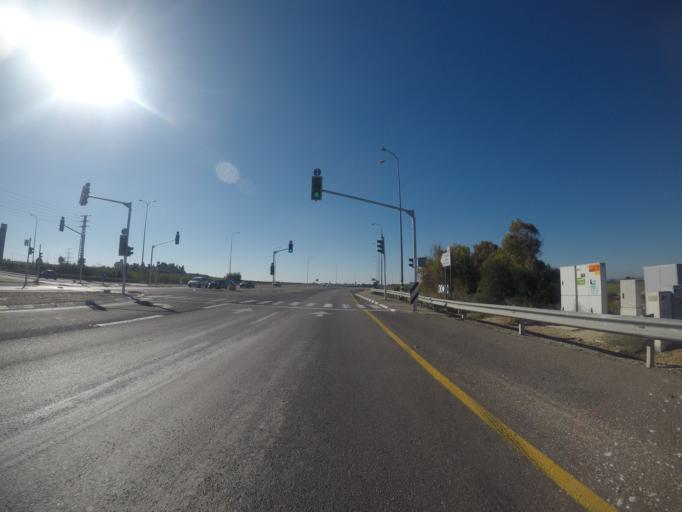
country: IL
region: Southern District
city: Ashdod
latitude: 31.7534
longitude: 34.6628
